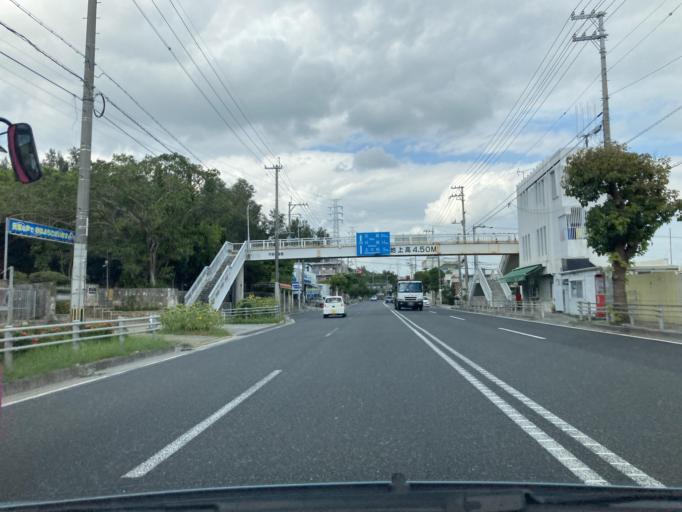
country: JP
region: Okinawa
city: Ginowan
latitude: 26.2481
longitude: 127.7821
